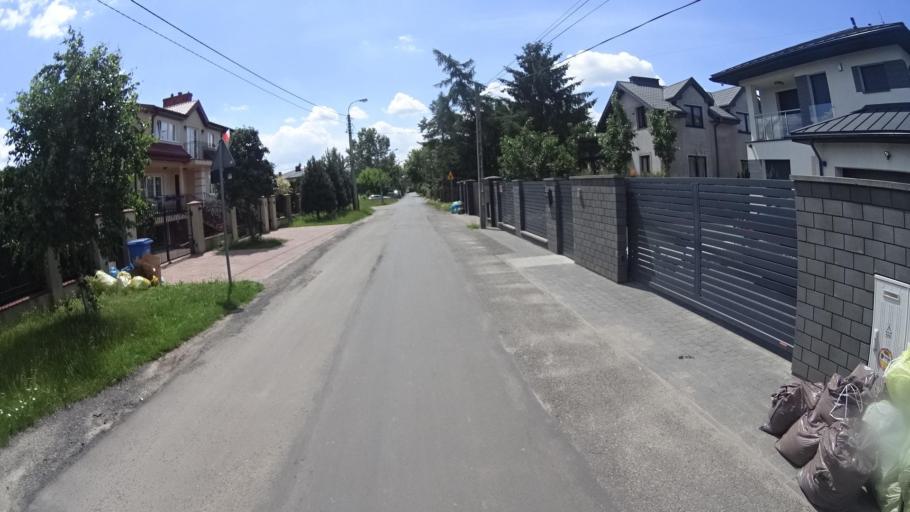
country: PL
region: Masovian Voivodeship
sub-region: Warszawa
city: Bemowo
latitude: 52.2459
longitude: 20.8865
